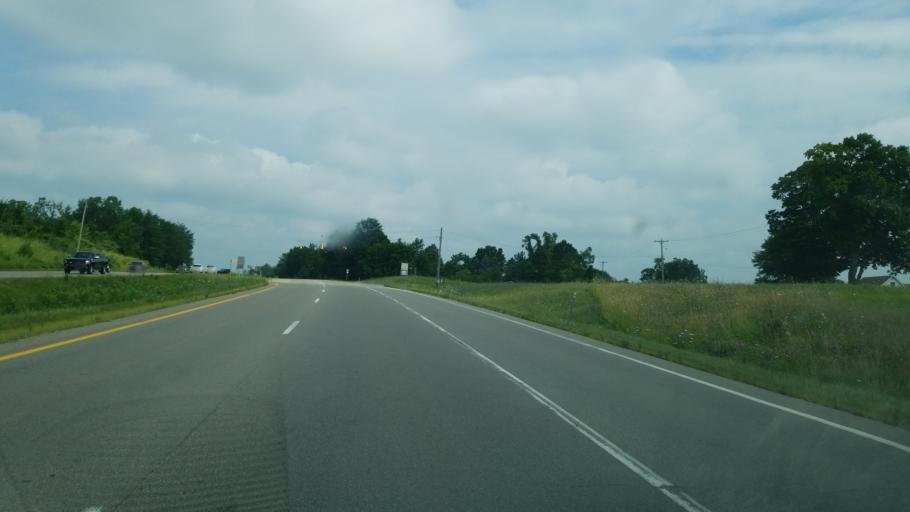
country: US
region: Michigan
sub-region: Kent County
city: Comstock Park
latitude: 43.0915
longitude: -85.6904
